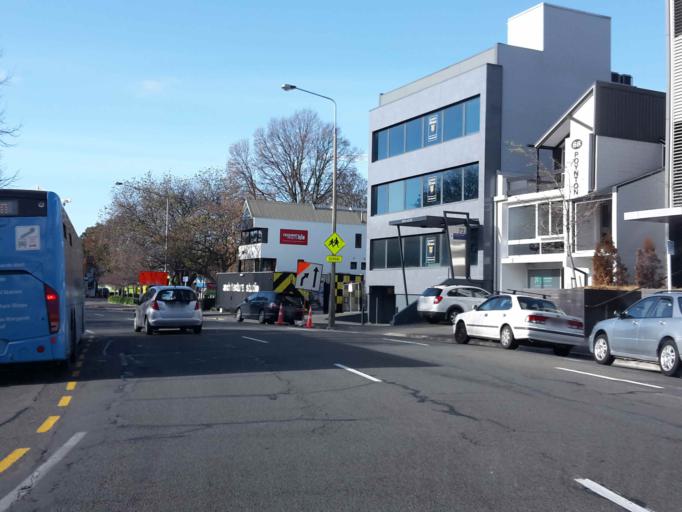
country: NZ
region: Canterbury
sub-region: Christchurch City
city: Christchurch
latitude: -43.5349
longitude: 172.6312
